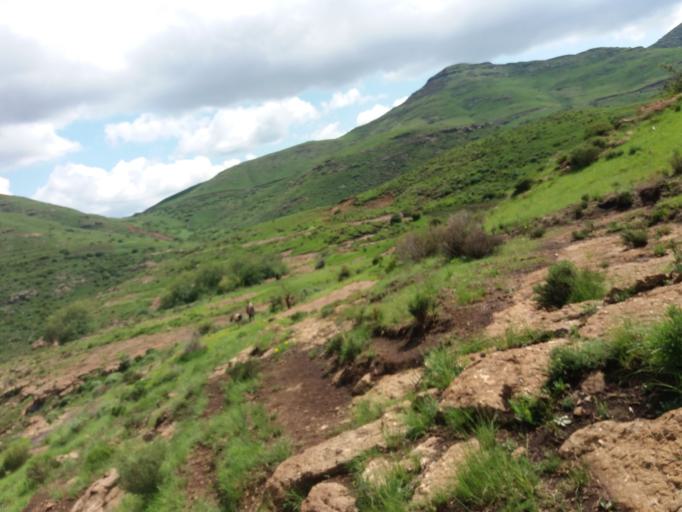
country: LS
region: Maseru
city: Nako
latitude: -29.6760
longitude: 27.9108
